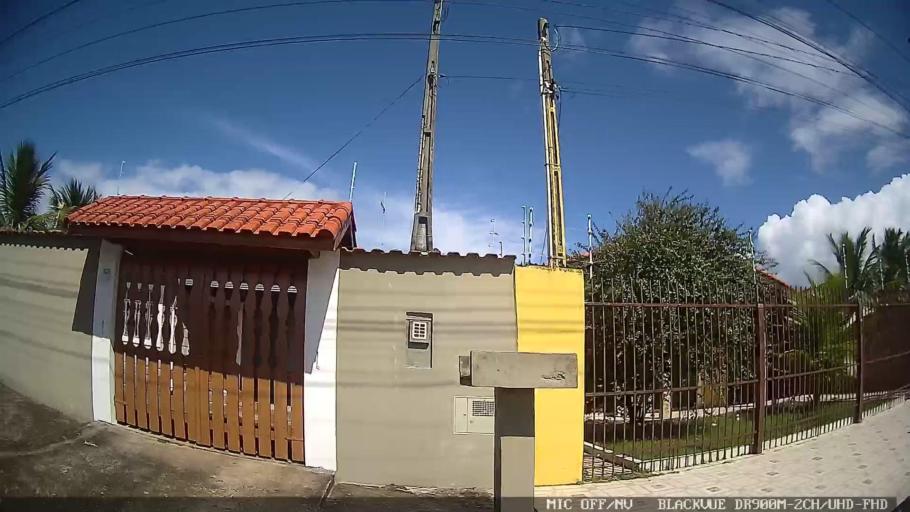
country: BR
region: Sao Paulo
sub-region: Itanhaem
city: Itanhaem
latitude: -24.2223
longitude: -46.8587
